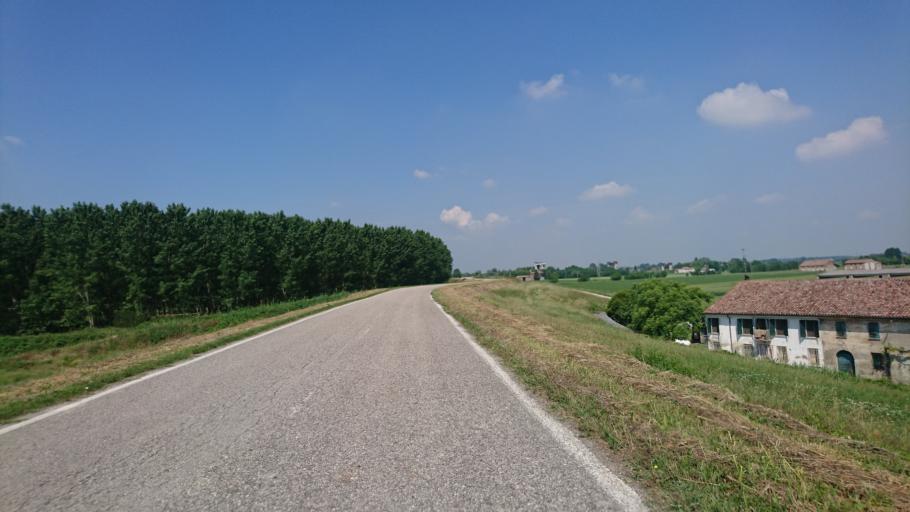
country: IT
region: Lombardy
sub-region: Provincia di Mantova
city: Sustinente
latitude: 45.0720
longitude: 10.9857
